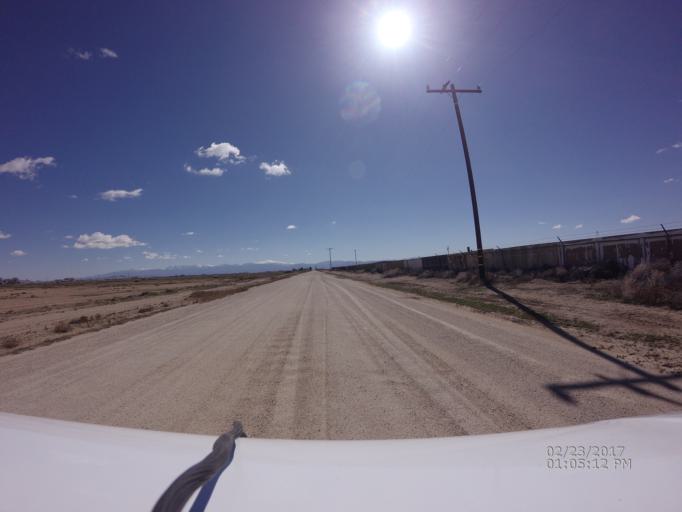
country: US
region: California
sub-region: Los Angeles County
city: Lancaster
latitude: 34.7610
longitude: -118.0146
